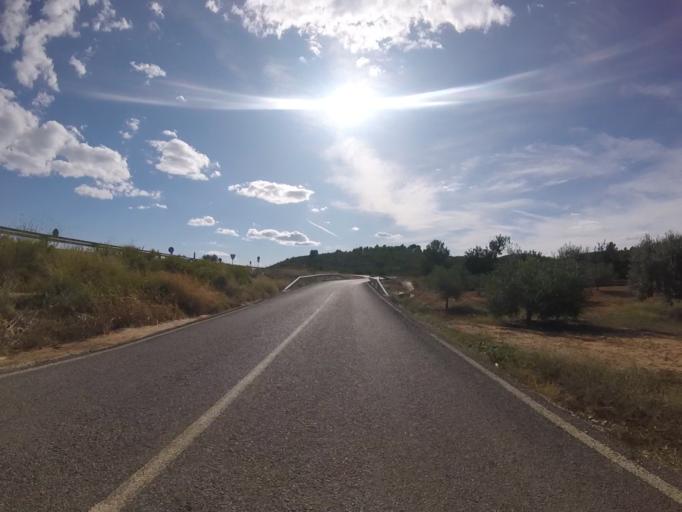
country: ES
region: Valencia
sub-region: Provincia de Castello
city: Alcala de Xivert
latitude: 40.2689
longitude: 0.2400
